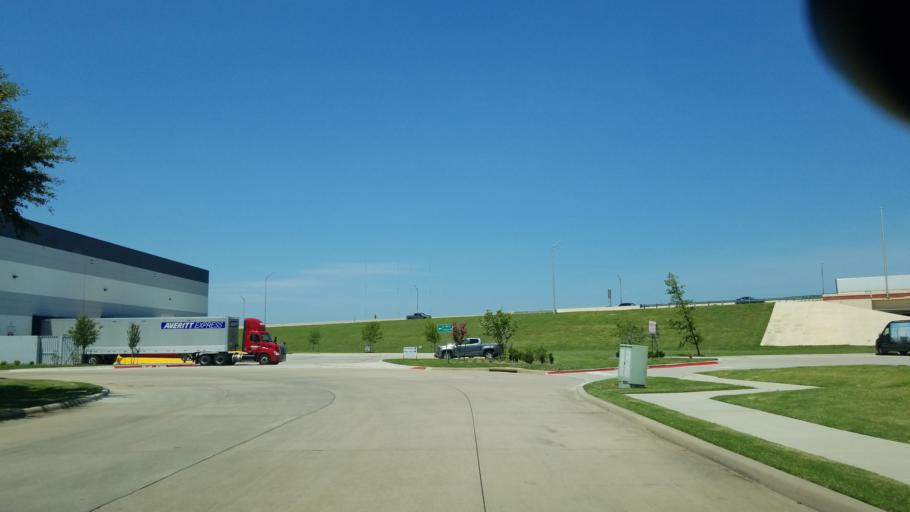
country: US
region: Texas
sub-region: Dallas County
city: Farmers Branch
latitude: 32.9454
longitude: -96.9265
